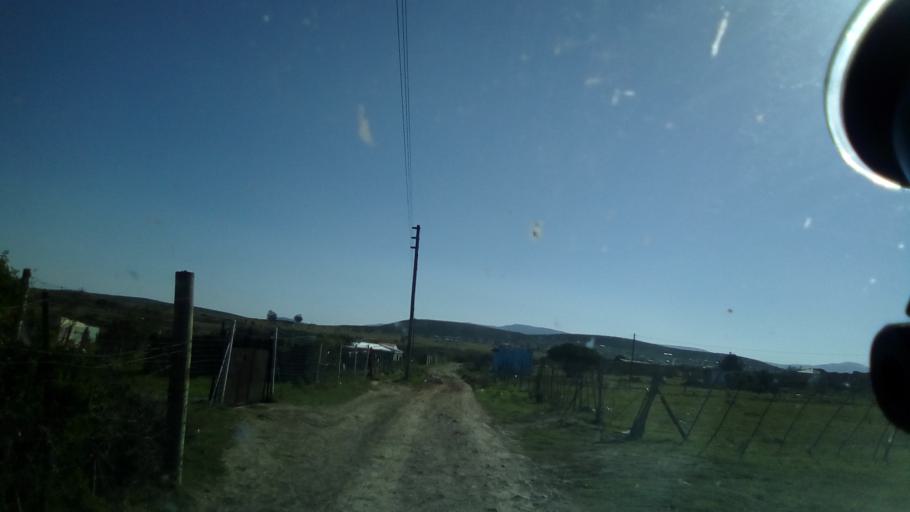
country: ZA
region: Eastern Cape
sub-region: Buffalo City Metropolitan Municipality
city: Bhisho
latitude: -32.8255
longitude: 27.3703
